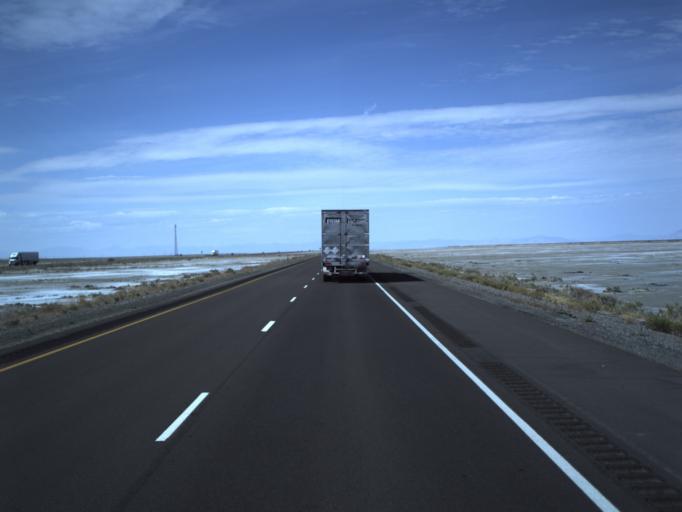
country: US
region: Utah
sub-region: Tooele County
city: Wendover
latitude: 40.7282
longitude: -113.3058
